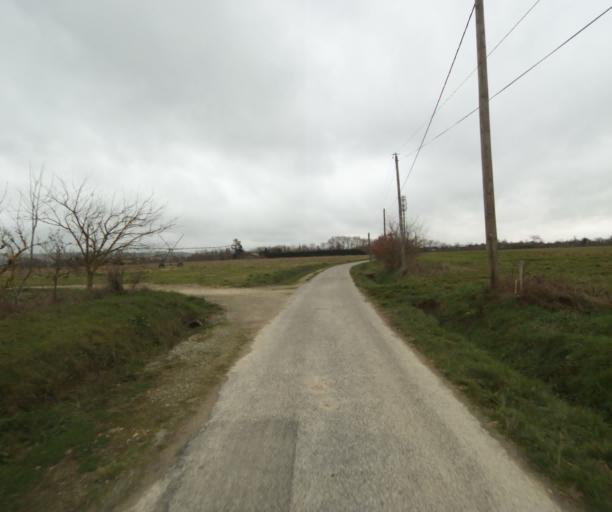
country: FR
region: Midi-Pyrenees
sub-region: Departement de l'Ariege
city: Mazeres
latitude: 43.2510
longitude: 1.6634
